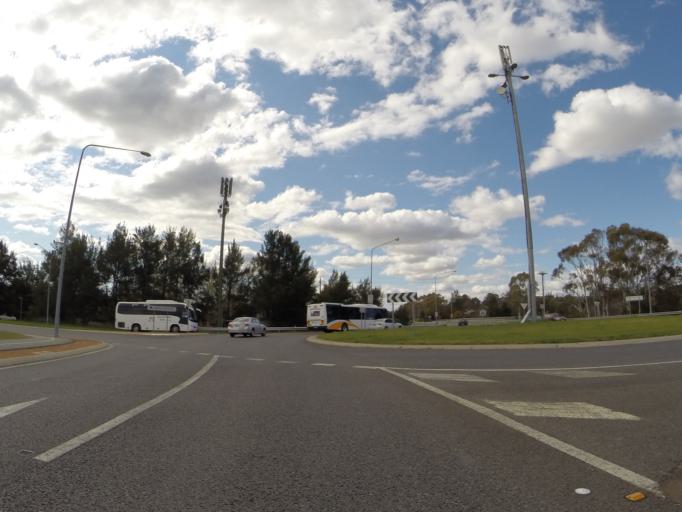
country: AU
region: Australian Capital Territory
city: Belconnen
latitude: -35.2136
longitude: 149.0866
